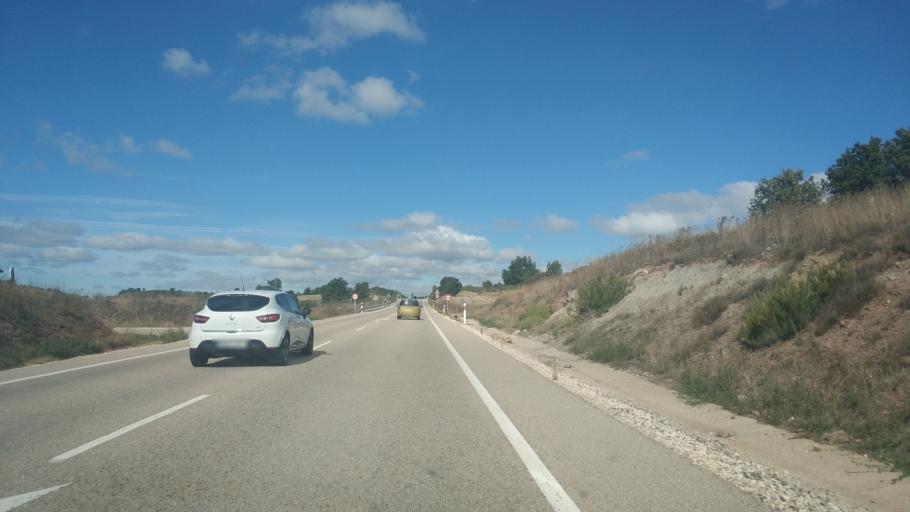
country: ES
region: Castille and Leon
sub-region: Provincia de Burgos
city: Cabezon de la Sierra
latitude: 41.8923
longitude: -3.2532
